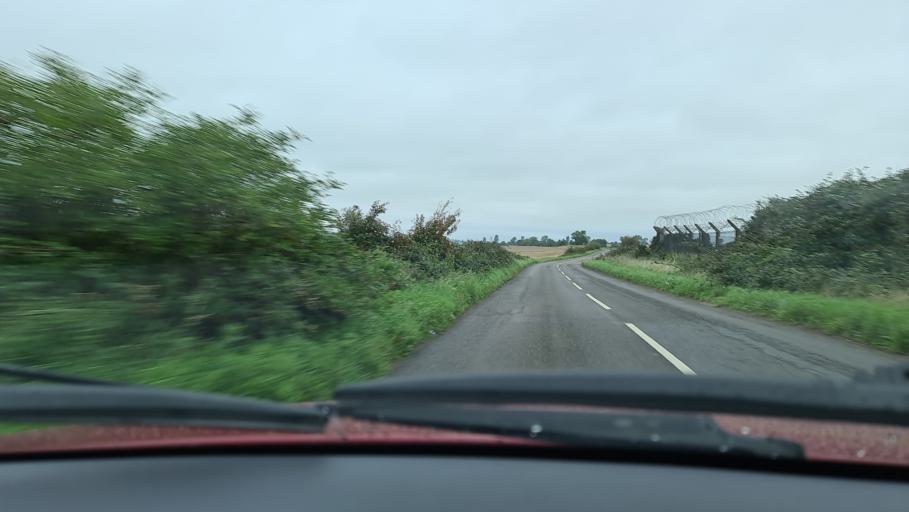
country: GB
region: England
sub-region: Oxfordshire
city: Somerton
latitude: 51.9346
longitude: -1.2764
